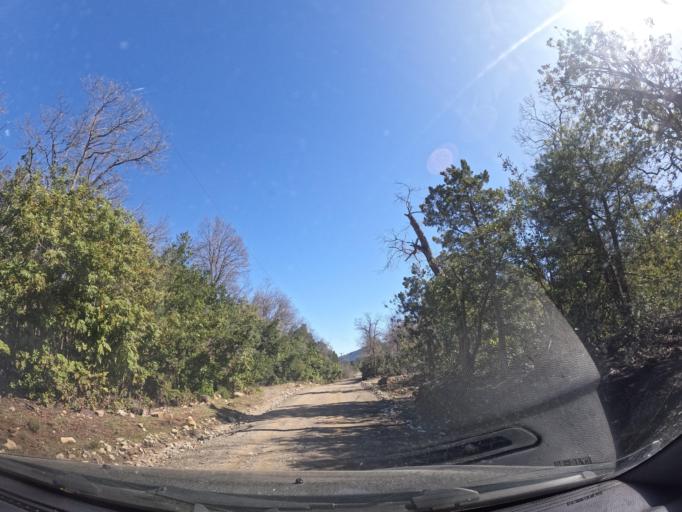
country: CL
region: Maule
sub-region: Provincia de Linares
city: Longavi
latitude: -36.2446
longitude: -71.3438
